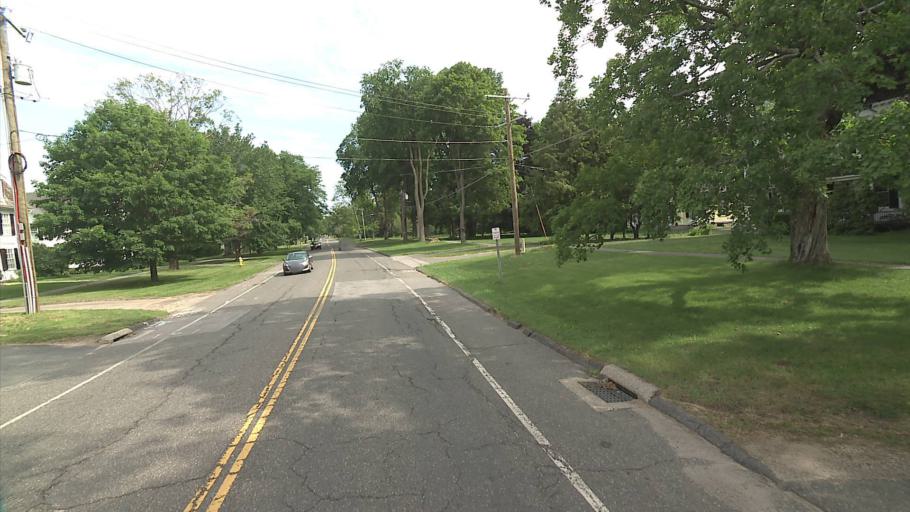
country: US
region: Connecticut
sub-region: Litchfield County
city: Litchfield
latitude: 41.7415
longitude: -73.1873
